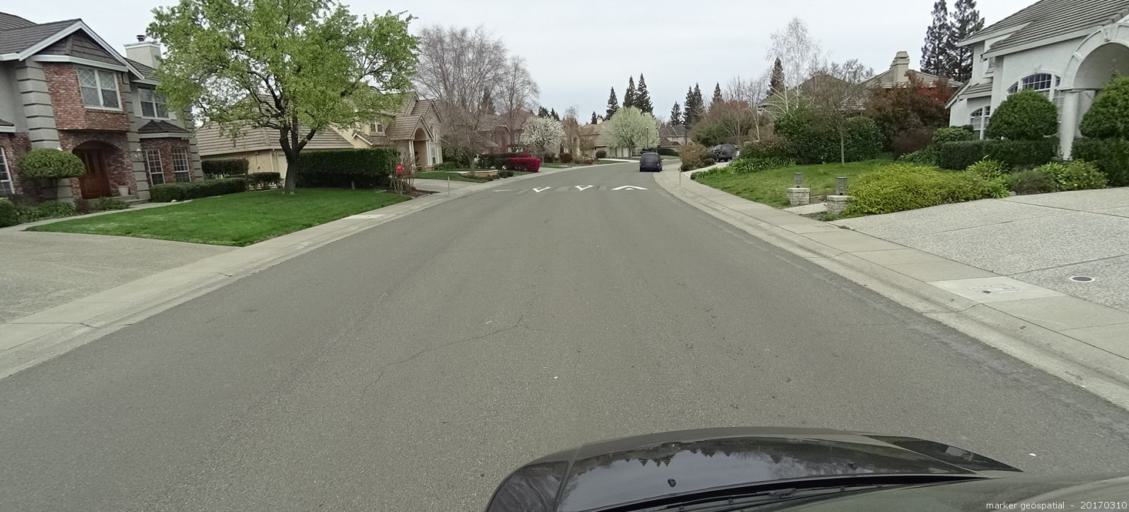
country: US
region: California
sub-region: Sacramento County
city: Parkway
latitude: 38.4797
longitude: -121.5329
